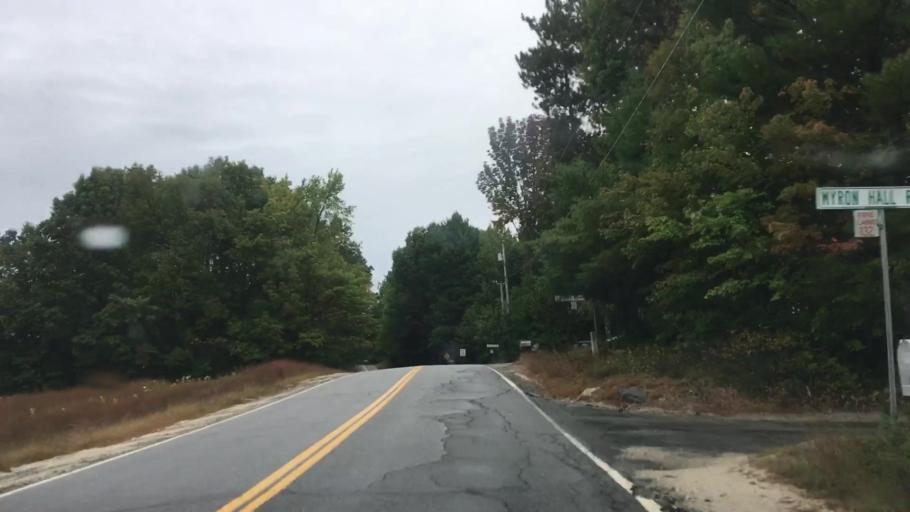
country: US
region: Maine
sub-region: Cumberland County
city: Raymond
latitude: 43.9743
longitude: -70.4694
